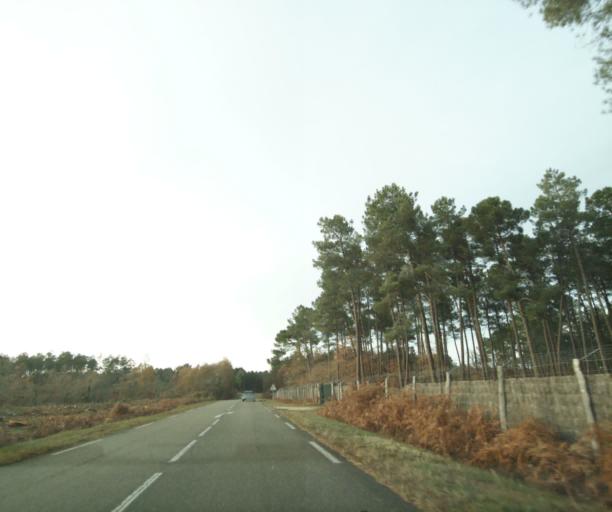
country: FR
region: Aquitaine
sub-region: Departement de la Gironde
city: Bazas
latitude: 44.2535
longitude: -0.2083
